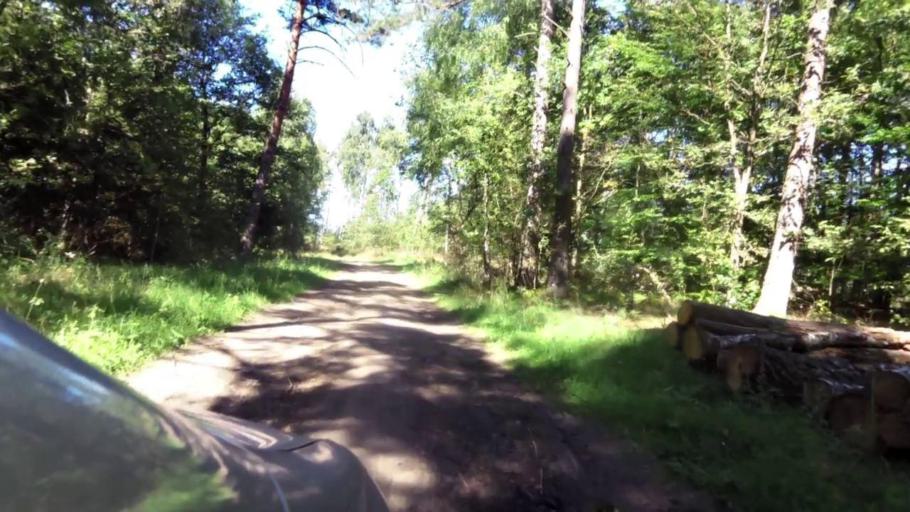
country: PL
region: West Pomeranian Voivodeship
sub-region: Powiat szczecinecki
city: Bialy Bor
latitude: 53.8316
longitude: 16.8704
